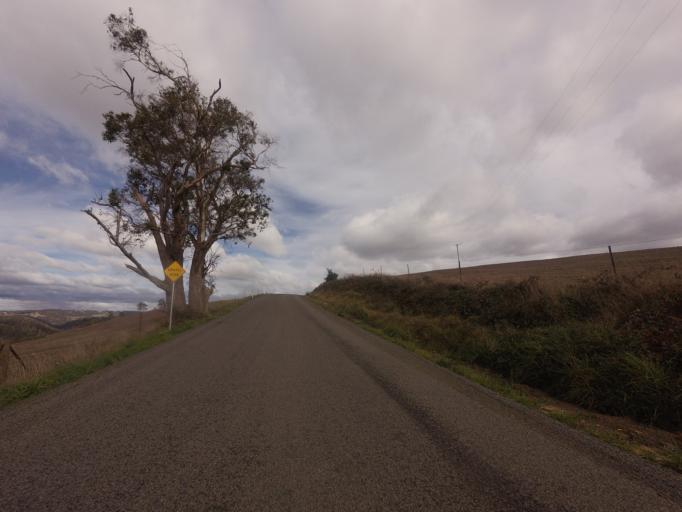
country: AU
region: Tasmania
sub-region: Brighton
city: Bridgewater
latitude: -42.4309
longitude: 147.3862
